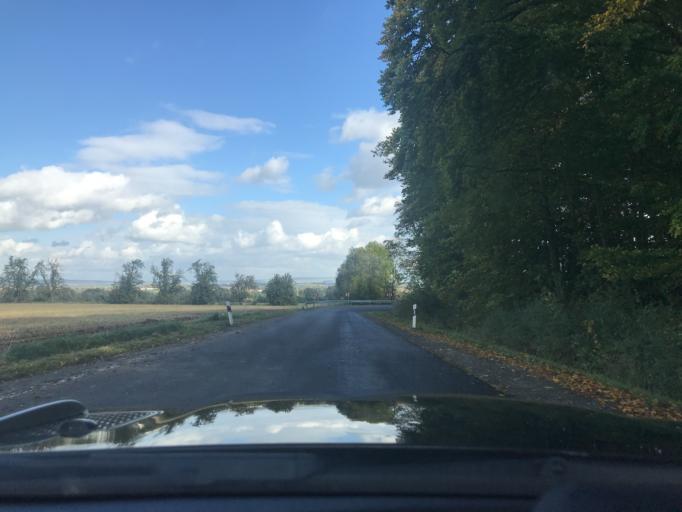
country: DE
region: Thuringia
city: Oberdorla
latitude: 51.1855
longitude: 10.4009
